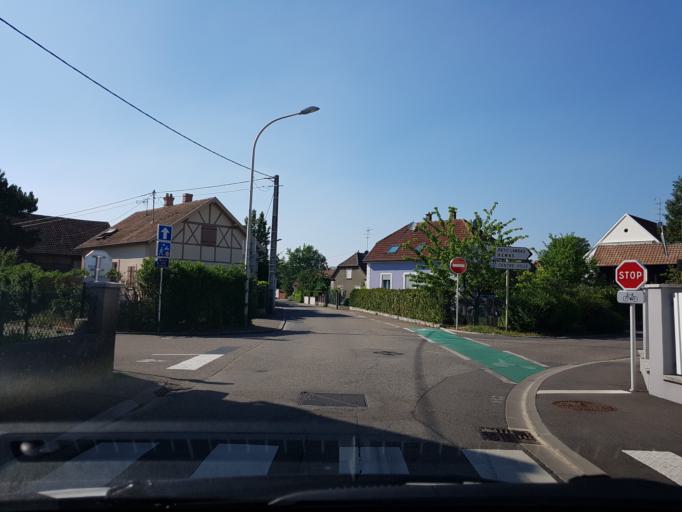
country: FR
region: Alsace
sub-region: Departement du Haut-Rhin
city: Habsheim
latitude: 47.7272
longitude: 7.4222
